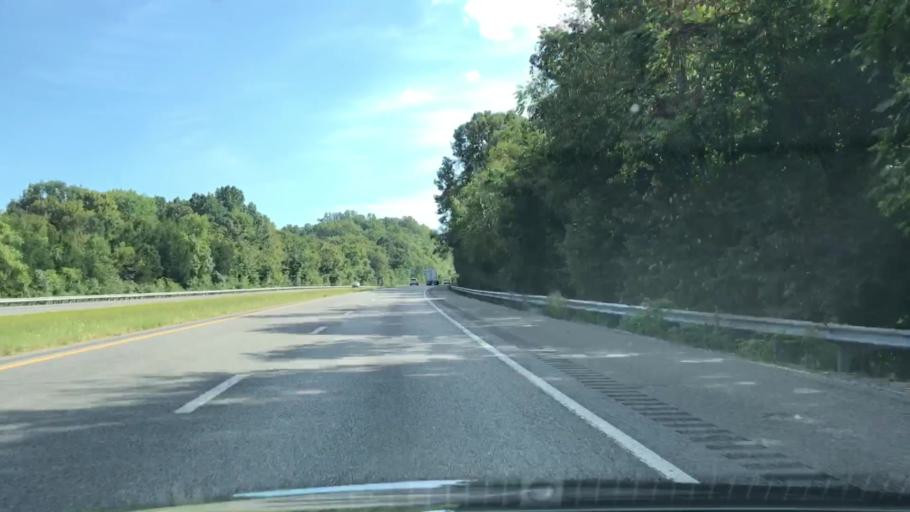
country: US
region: Alabama
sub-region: Limestone County
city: Ardmore
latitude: 35.1235
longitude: -86.8776
